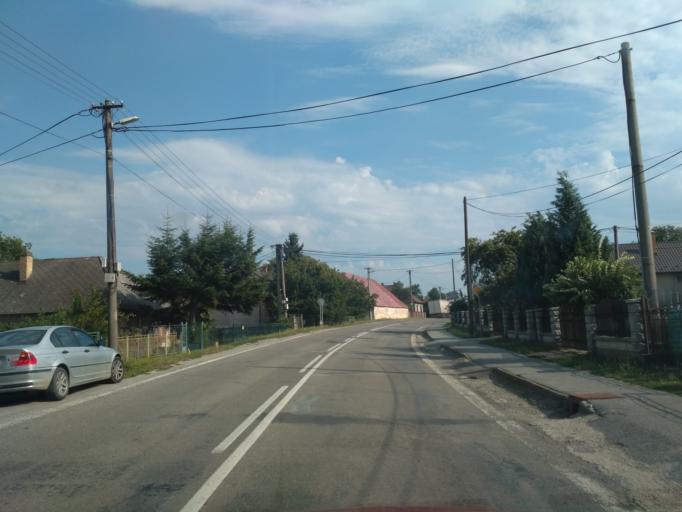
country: SK
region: Kosicky
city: Kosice
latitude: 48.8277
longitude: 21.2967
